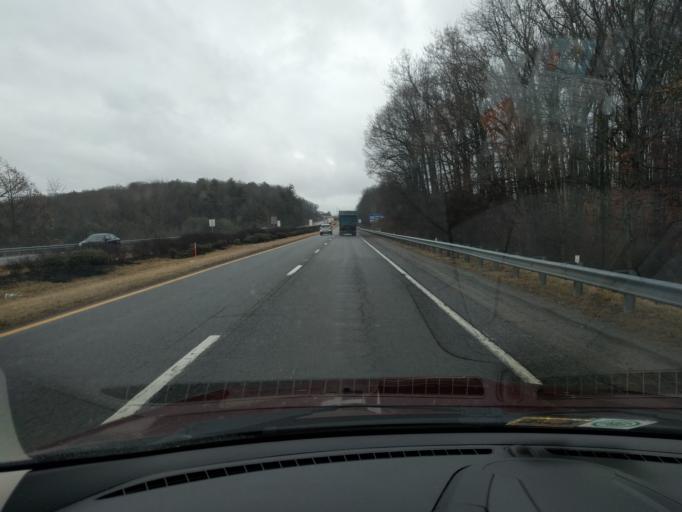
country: US
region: Virginia
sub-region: Montgomery County
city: Merrimac
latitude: 37.2035
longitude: -80.4185
